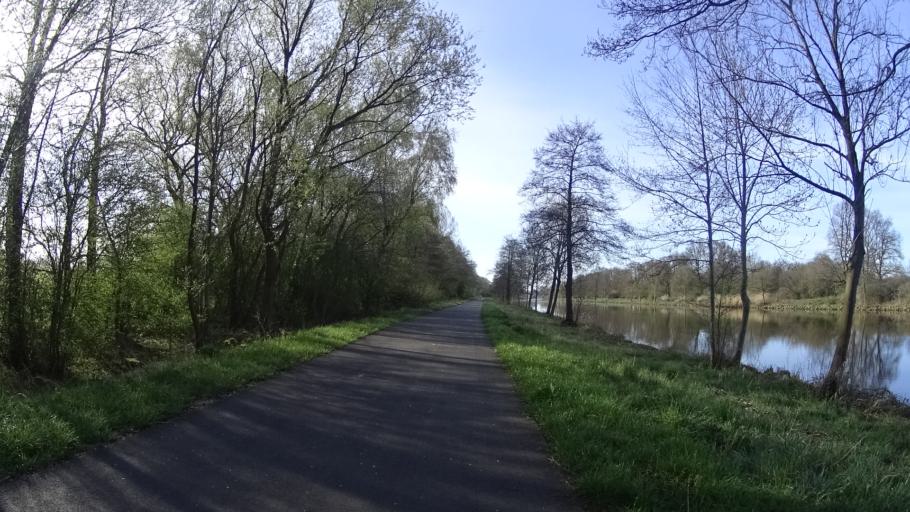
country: DE
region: Lower Saxony
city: Haren
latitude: 52.8043
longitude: 7.2602
